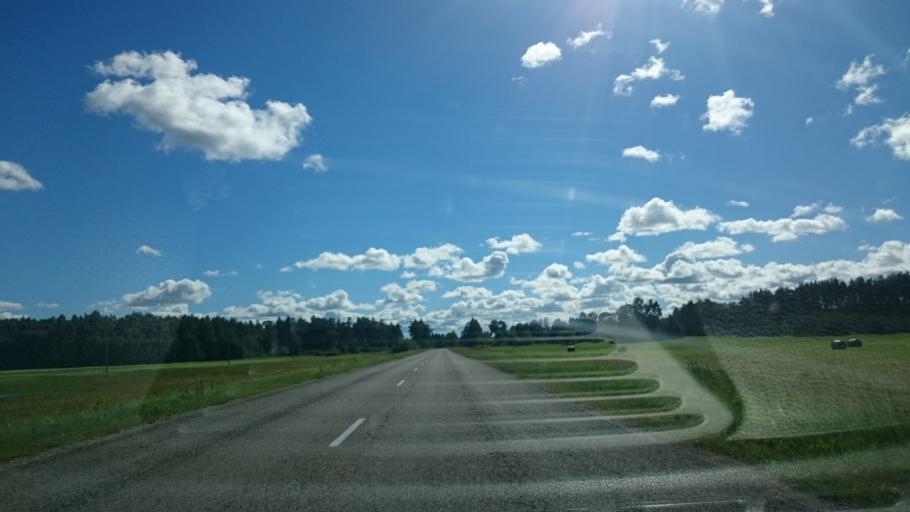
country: LV
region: Aizpute
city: Aizpute
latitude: 56.7855
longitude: 21.6472
